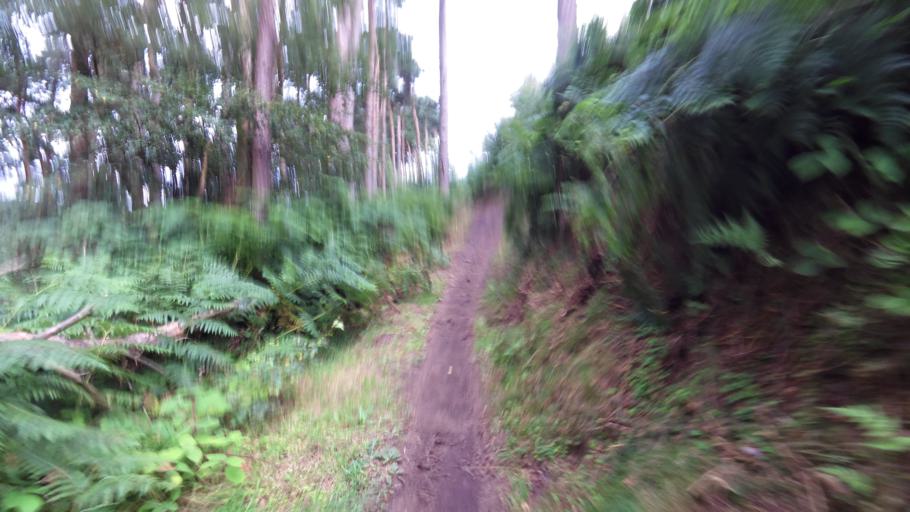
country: GB
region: England
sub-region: North Yorkshire
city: Thornton Dale
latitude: 54.2909
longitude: -0.6789
